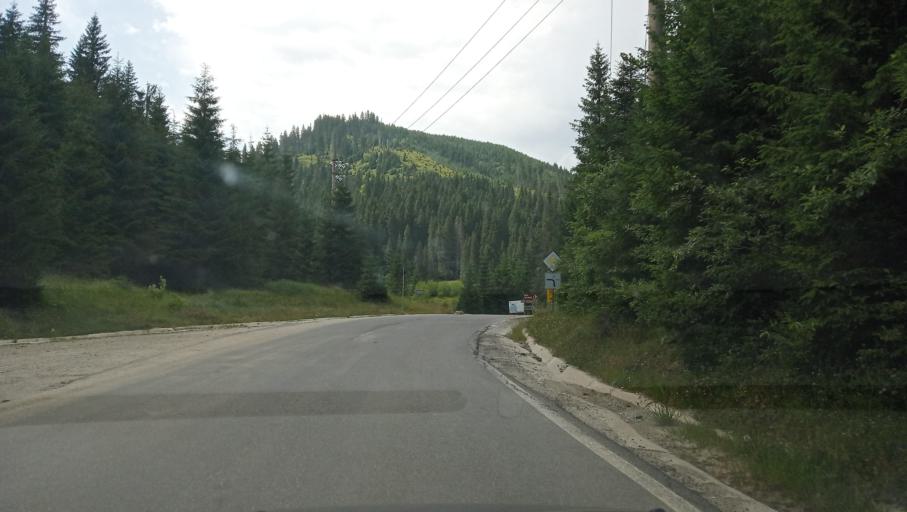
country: RO
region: Dambovita
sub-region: Comuna Moroeni
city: Glod
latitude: 45.3351
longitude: 25.4282
